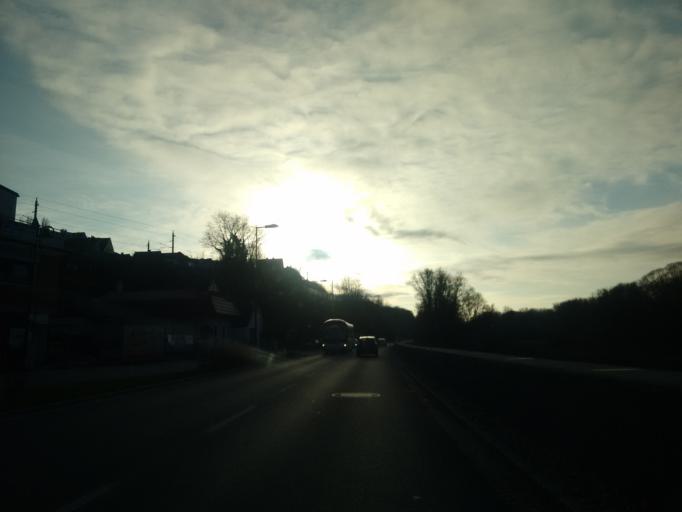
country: AT
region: Lower Austria
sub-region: Politischer Bezirk Melk
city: Melk
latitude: 48.2253
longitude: 15.3254
